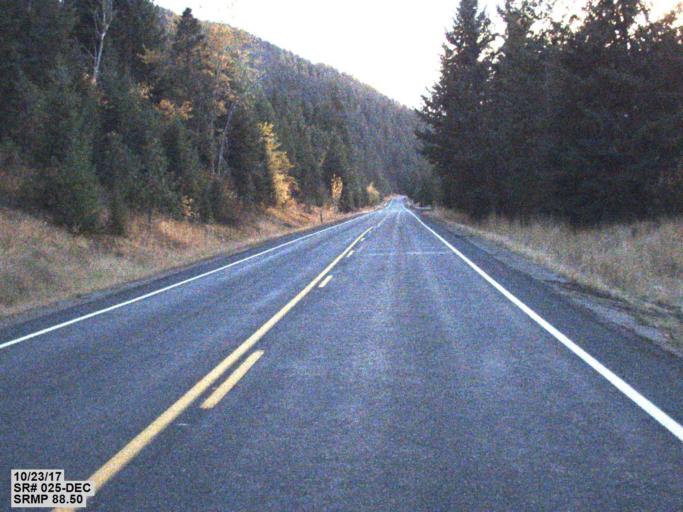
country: US
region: Washington
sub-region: Stevens County
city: Kettle Falls
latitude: 48.6782
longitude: -118.0180
